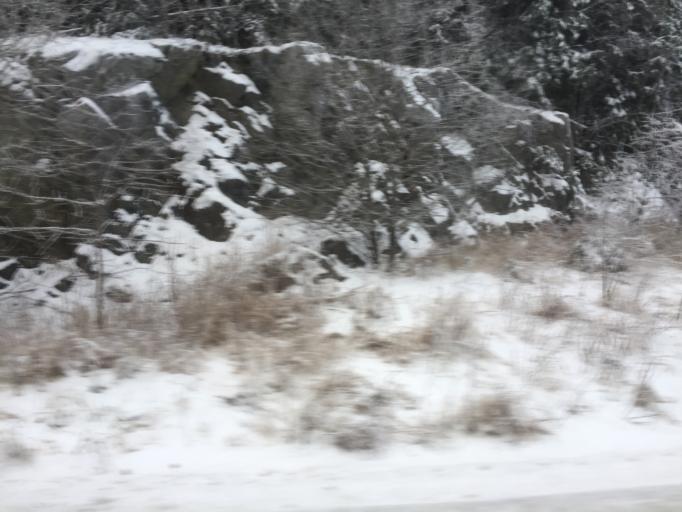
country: NO
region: Akershus
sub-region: Oppegard
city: Kolbotn
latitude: 59.7546
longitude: 10.7822
